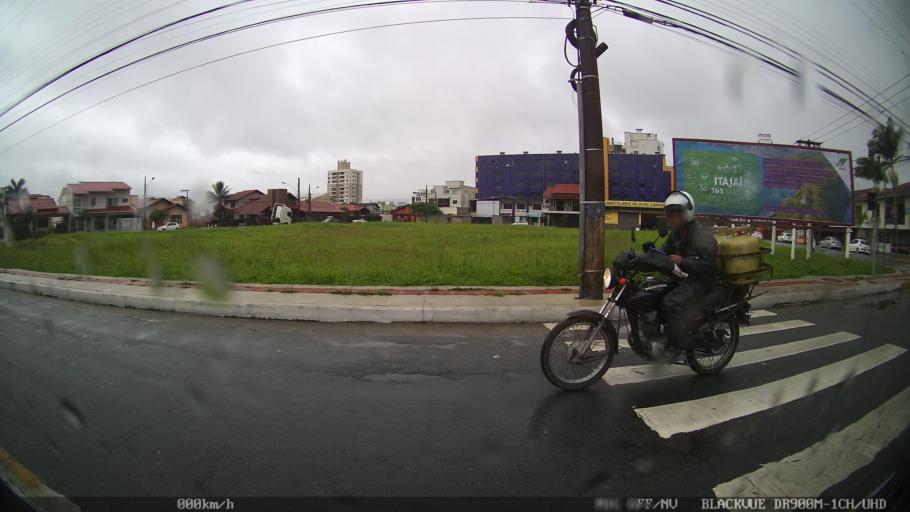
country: BR
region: Santa Catarina
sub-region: Itajai
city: Itajai
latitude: -26.9216
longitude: -48.6776
